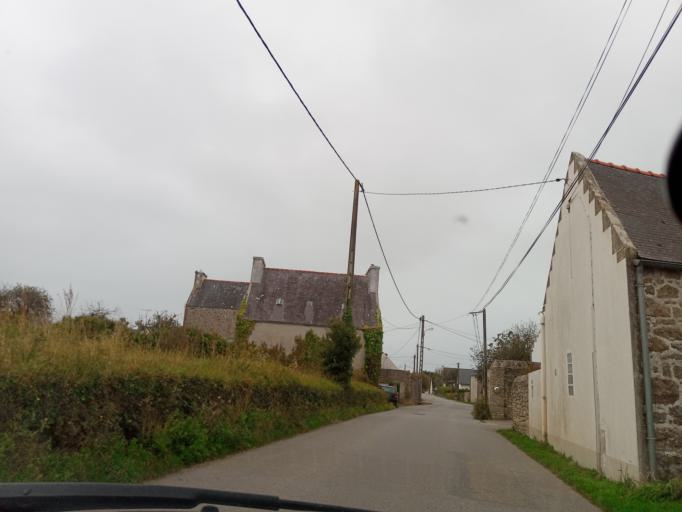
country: FR
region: Brittany
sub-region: Departement du Finistere
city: Esquibien
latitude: 48.0215
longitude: -4.5637
